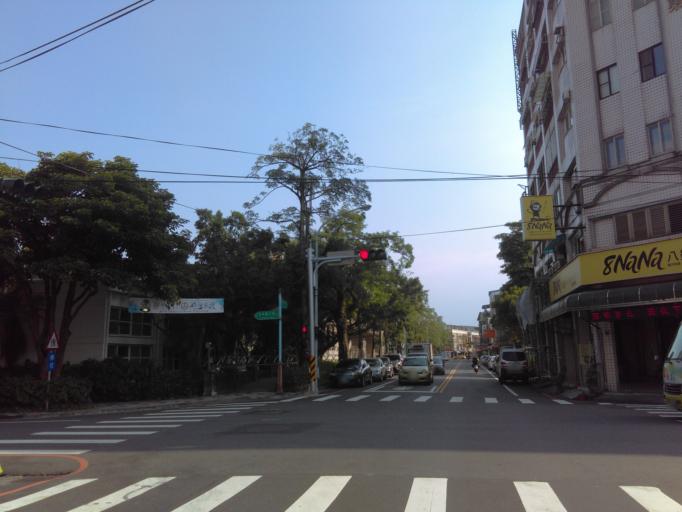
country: TW
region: Taiwan
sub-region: Yilan
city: Yilan
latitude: 24.7453
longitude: 121.7523
